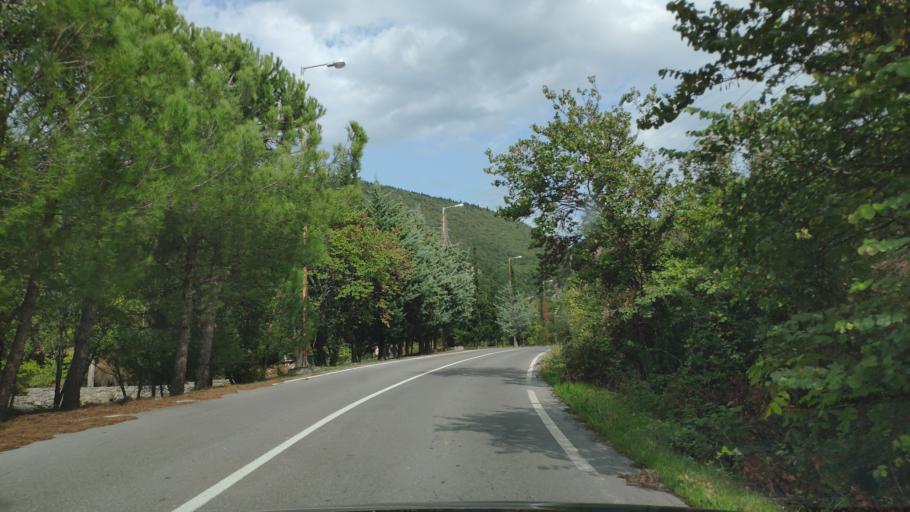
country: GR
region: Central Greece
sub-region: Nomos Fthiotidos
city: Anthili
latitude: 38.7474
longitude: 22.4533
